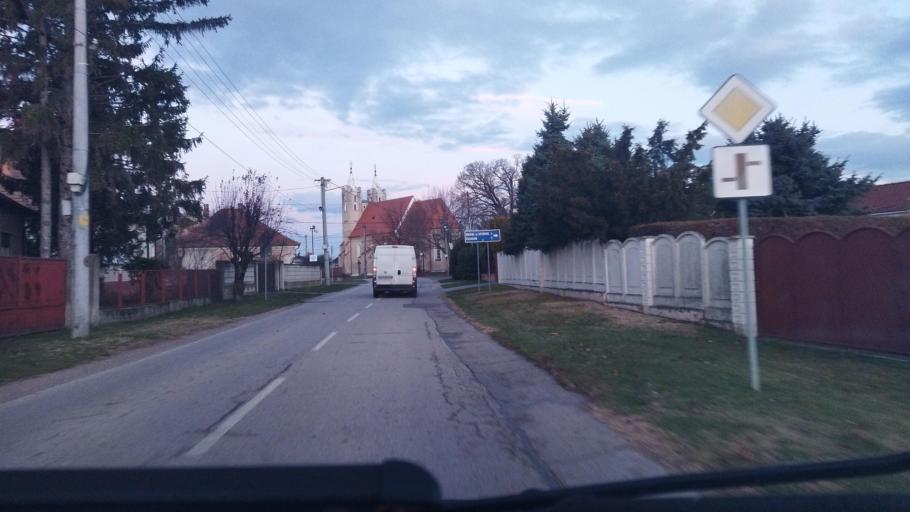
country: SK
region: Trnavsky
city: Dunajska Streda
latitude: 47.9947
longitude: 17.4850
